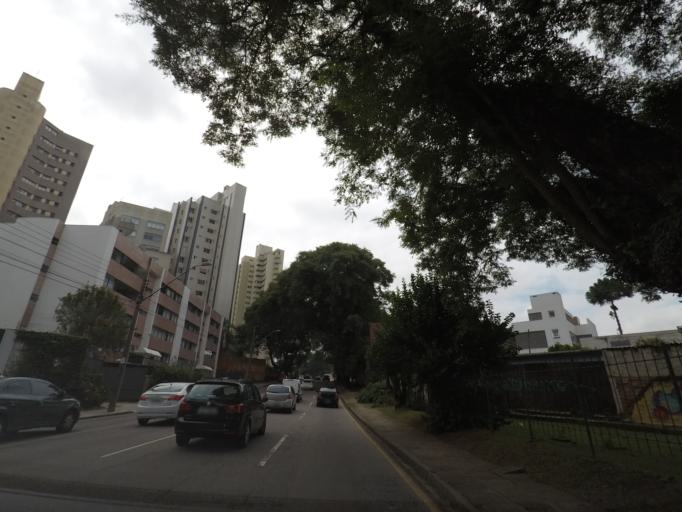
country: BR
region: Parana
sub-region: Curitiba
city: Curitiba
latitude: -25.4550
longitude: -49.2852
